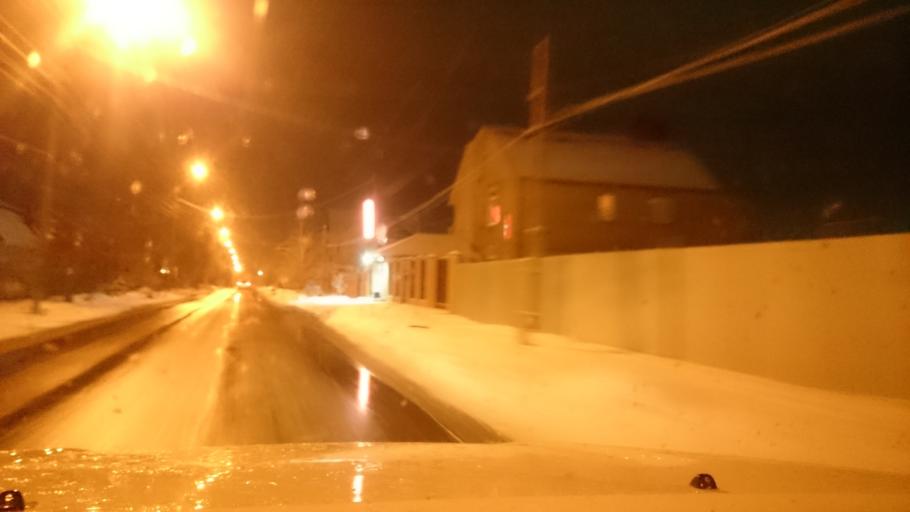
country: RU
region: Tula
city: Tula
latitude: 54.2033
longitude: 37.5553
